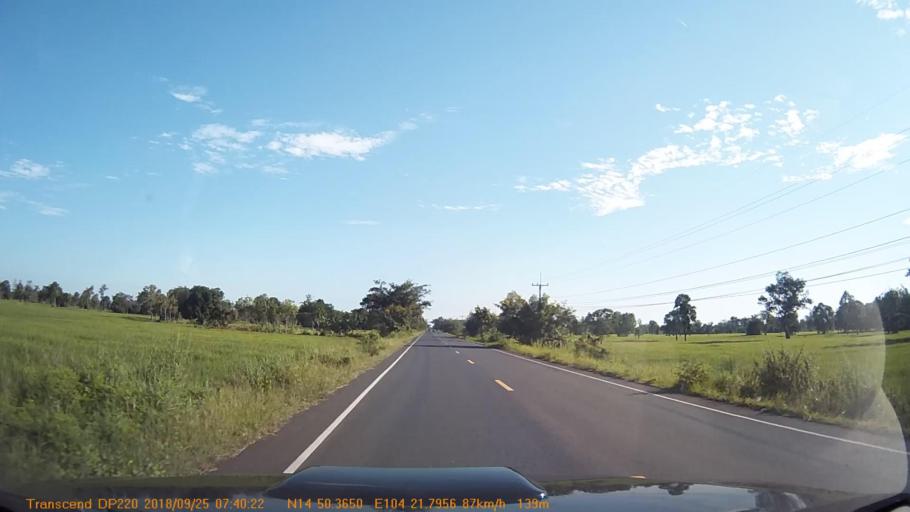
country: TH
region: Sisaket
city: Phayu
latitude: 14.8400
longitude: 104.3634
